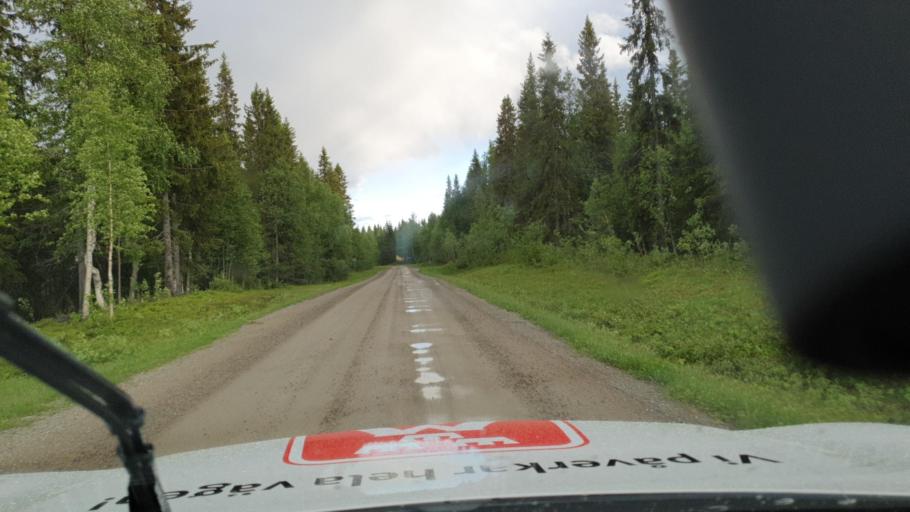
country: SE
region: Vaesterbotten
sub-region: Storumans Kommun
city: Storuman
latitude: 64.8028
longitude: 16.9706
